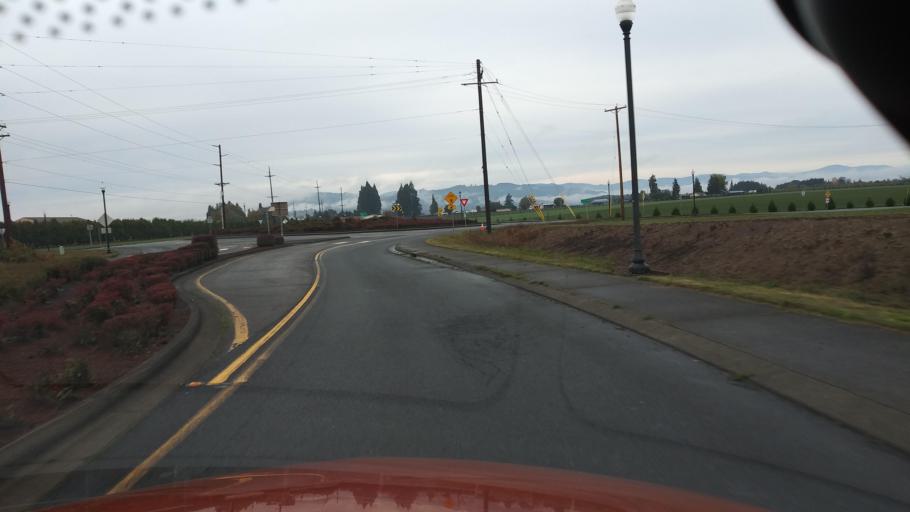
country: US
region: Oregon
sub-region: Washington County
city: Cornelius
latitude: 45.5516
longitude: -123.0721
